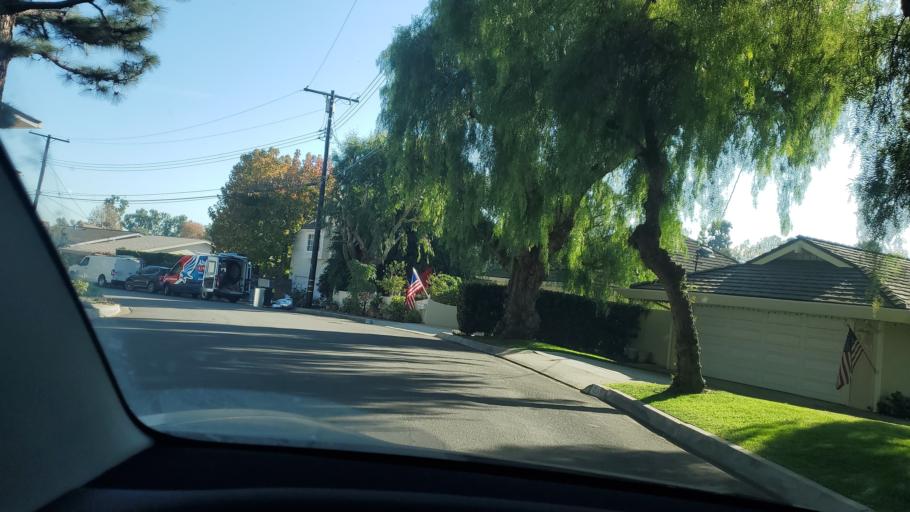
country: US
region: California
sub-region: Los Angeles County
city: Rolling Hills Estates
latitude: 33.7967
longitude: -118.3607
